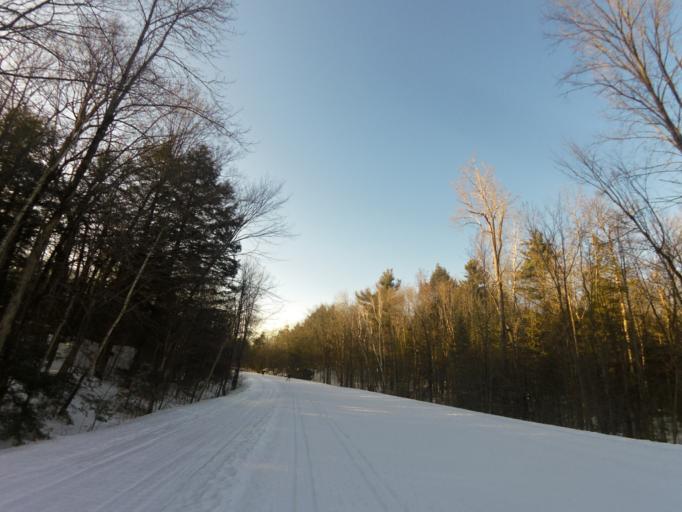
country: CA
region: Quebec
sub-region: Outaouais
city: Gatineau
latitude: 45.5244
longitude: -75.8351
